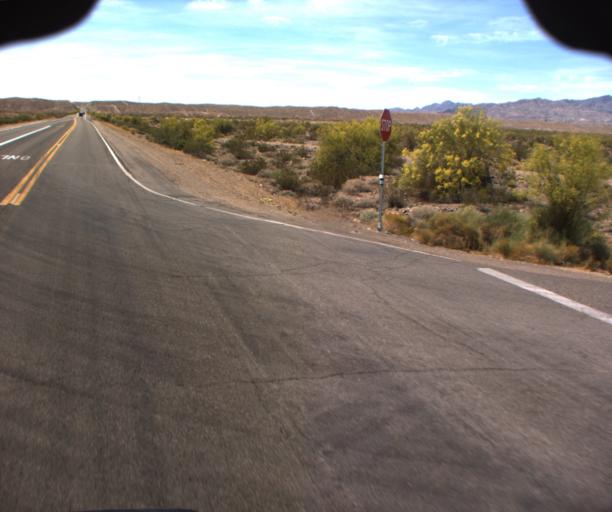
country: US
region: Arizona
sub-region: Mohave County
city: Lake Havasu City
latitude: 34.4160
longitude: -114.1958
